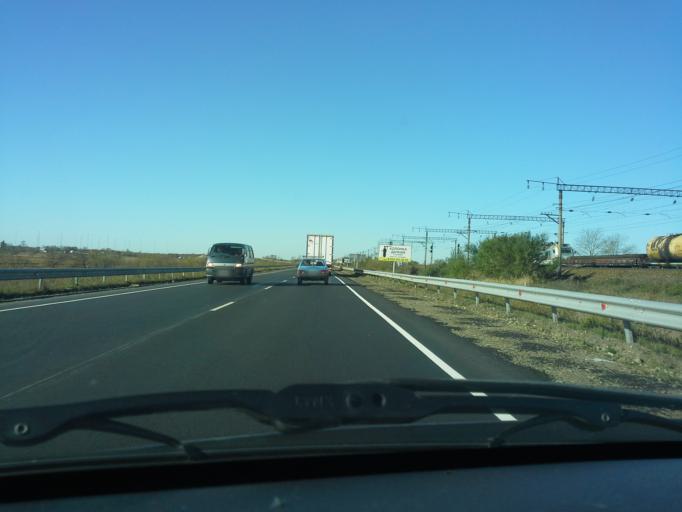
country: RU
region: Jewish Autonomous Oblast
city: Priamurskiy
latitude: 48.5261
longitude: 134.9358
